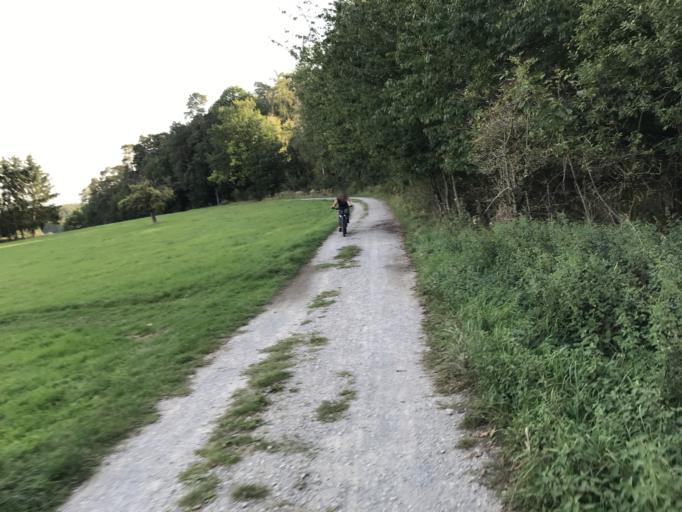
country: DE
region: Hesse
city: Lollar
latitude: 50.6402
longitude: 8.6539
